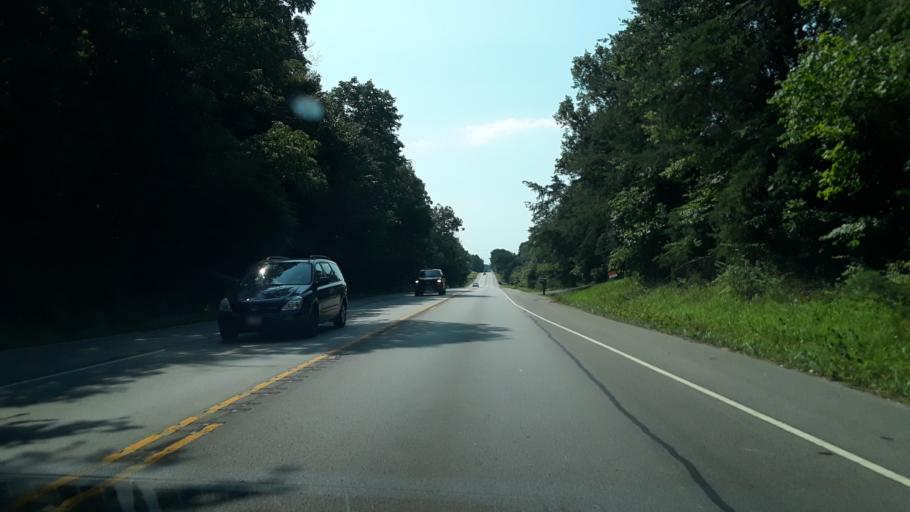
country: US
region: Indiana
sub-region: Clark County
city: Sellersburg
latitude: 38.4198
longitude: -85.8019
